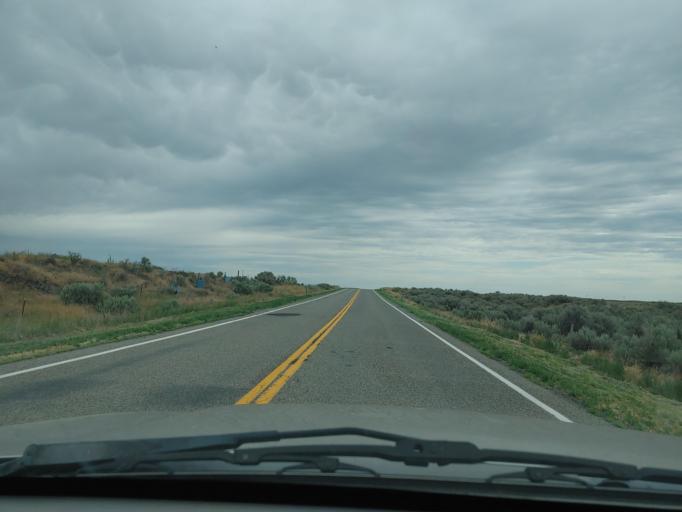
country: US
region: Idaho
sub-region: Lincoln County
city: Shoshone
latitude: 43.0636
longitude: -114.1227
